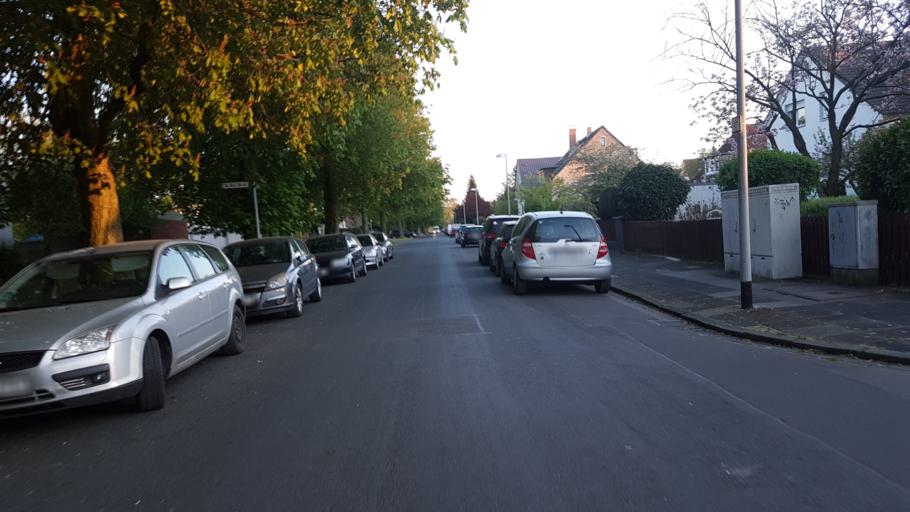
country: DE
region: Lower Saxony
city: Langenhagen
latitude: 52.4208
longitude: 9.7718
